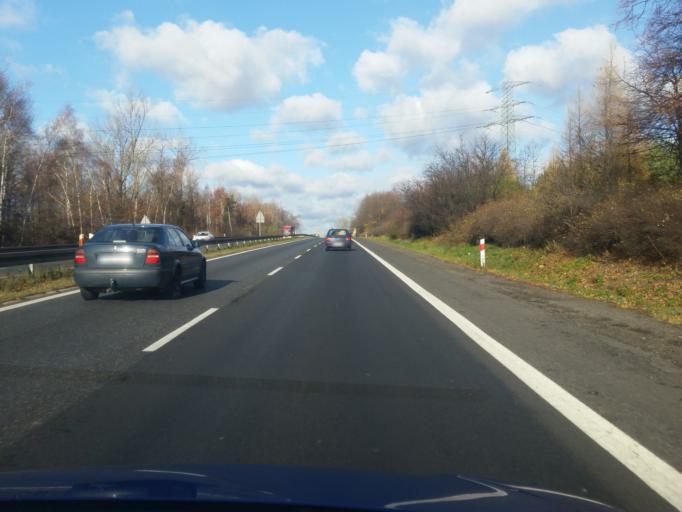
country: PL
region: Silesian Voivodeship
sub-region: Powiat czestochowski
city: Huta Stara B
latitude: 50.7402
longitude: 19.1571
